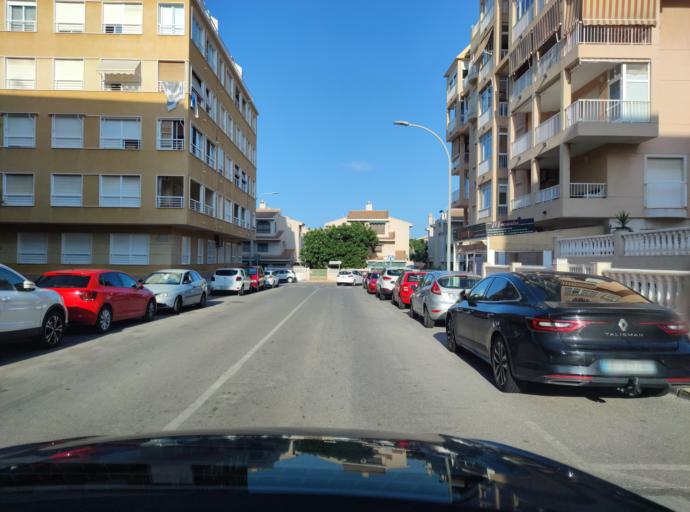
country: ES
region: Valencia
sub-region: Provincia de Alicante
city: Guardamar del Segura
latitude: 38.0827
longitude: -0.6521
